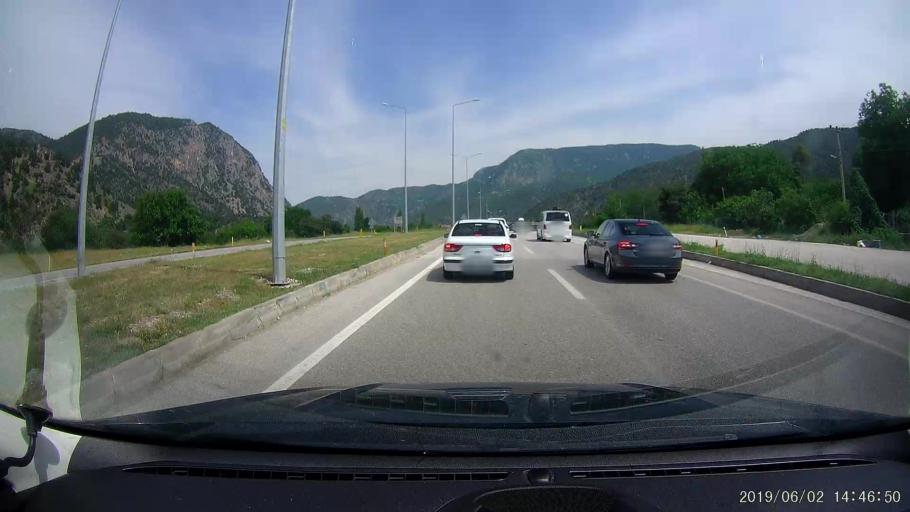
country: TR
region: Corum
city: Hacihamza
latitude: 41.0733
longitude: 34.4553
